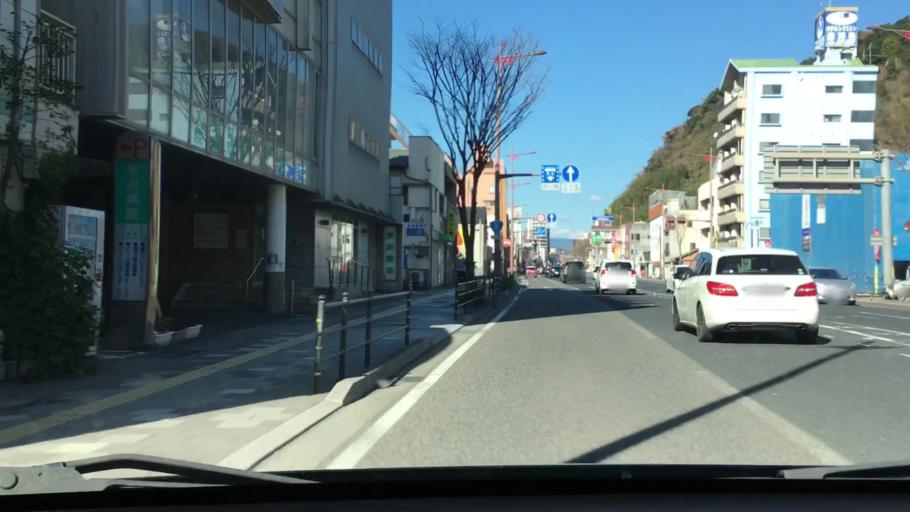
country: JP
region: Kagoshima
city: Kagoshima-shi
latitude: 31.5936
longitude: 130.5436
